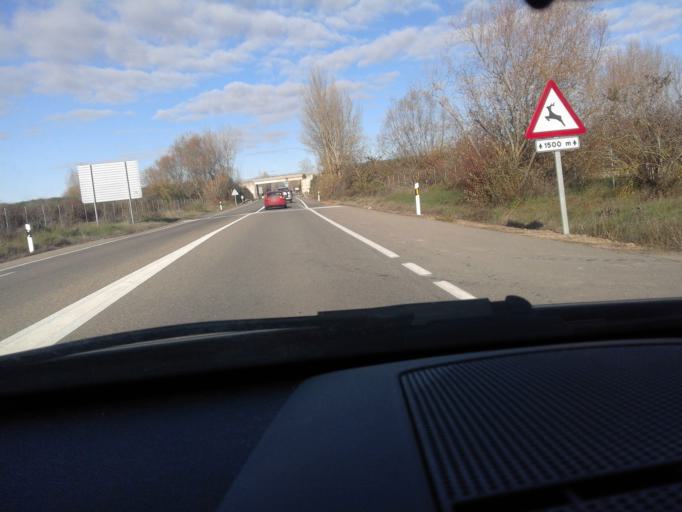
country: ES
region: Castille and Leon
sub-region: Provincia de Palencia
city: Carrion de los Condes
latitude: 42.3426
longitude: -4.6150
